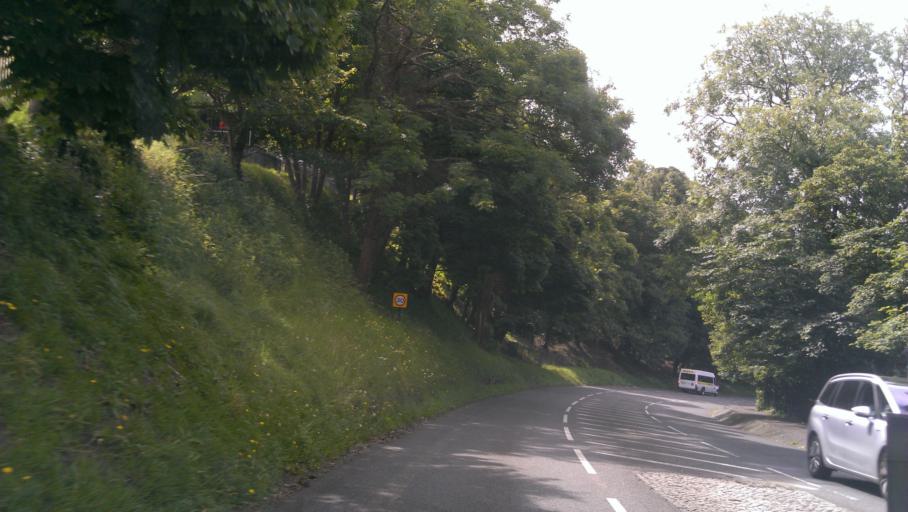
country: GB
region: England
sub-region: Kent
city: Dover
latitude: 51.1310
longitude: 1.3189
